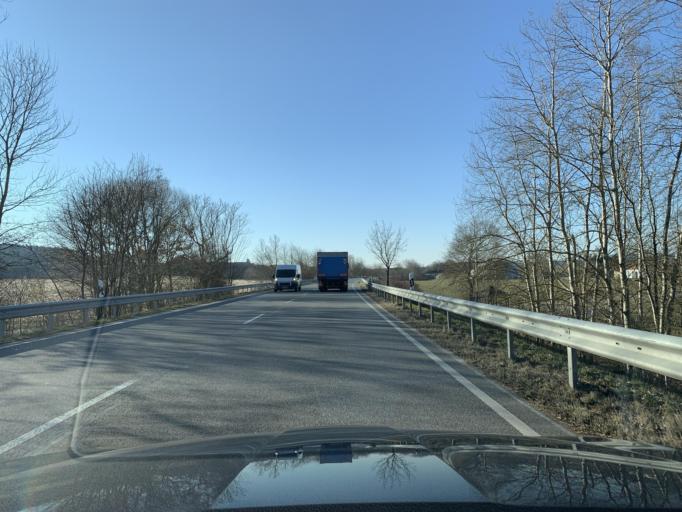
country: DE
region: Bavaria
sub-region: Upper Palatinate
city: Schonthal
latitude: 49.3320
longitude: 12.6189
